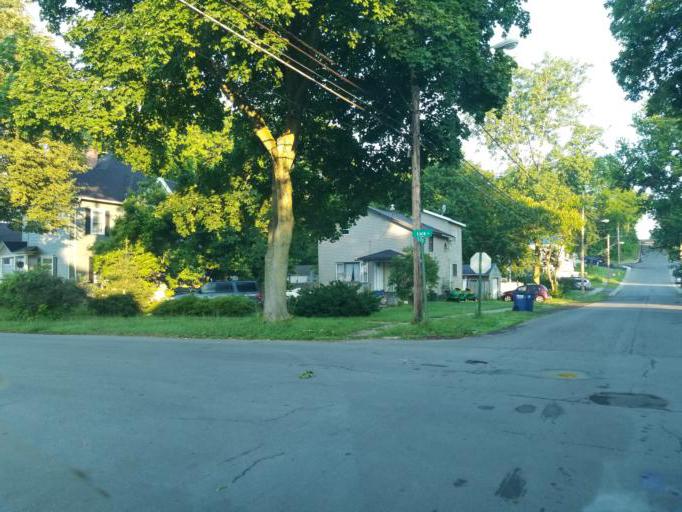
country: US
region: New York
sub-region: Wayne County
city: Clyde
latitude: 43.0872
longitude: -76.8717
